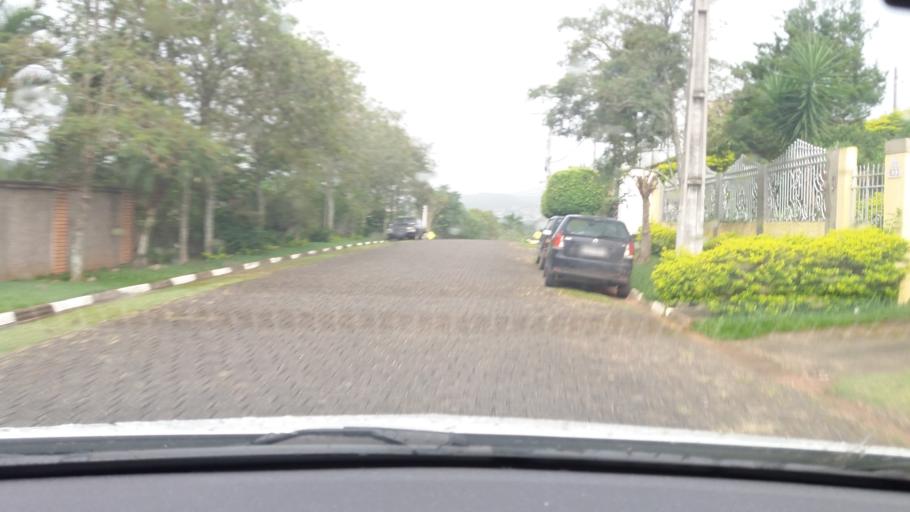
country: BR
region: Sao Paulo
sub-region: Bom Jesus Dos Perdoes
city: Bom Jesus dos Perdoes
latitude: -23.1661
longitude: -46.4530
